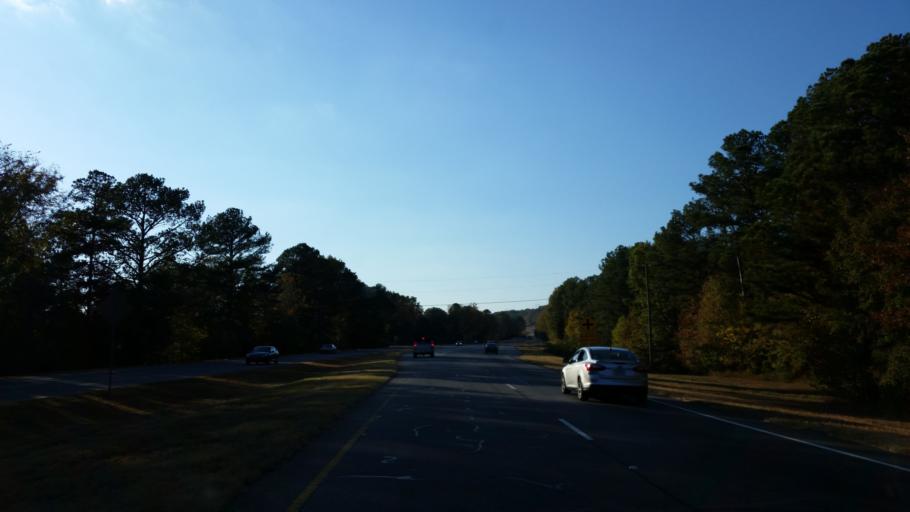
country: US
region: Georgia
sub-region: Bartow County
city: Cartersville
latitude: 34.2193
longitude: -84.8754
